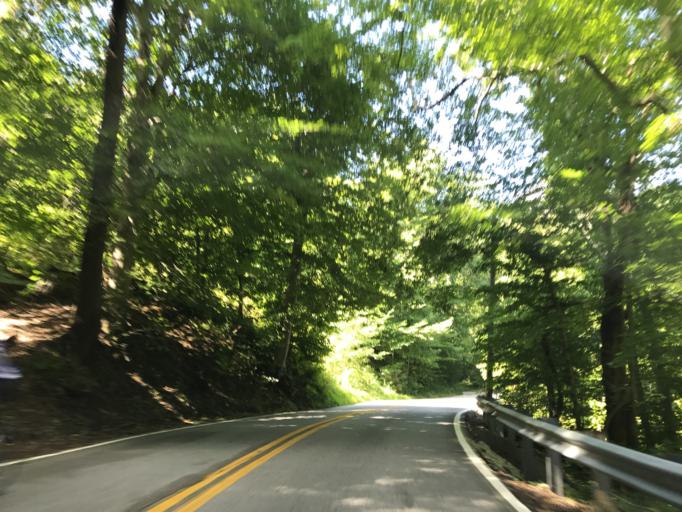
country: US
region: Maryland
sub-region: Howard County
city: Ilchester
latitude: 39.2556
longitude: -76.7661
